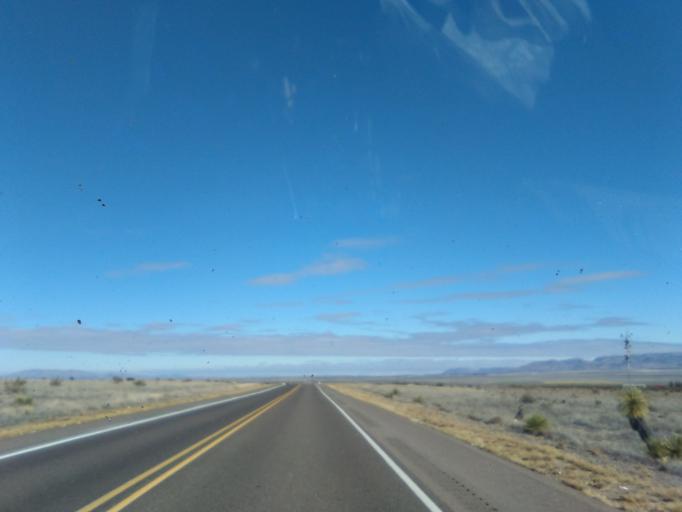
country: US
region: New Mexico
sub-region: Dona Ana County
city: Hatch
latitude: 32.5765
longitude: -107.3954
